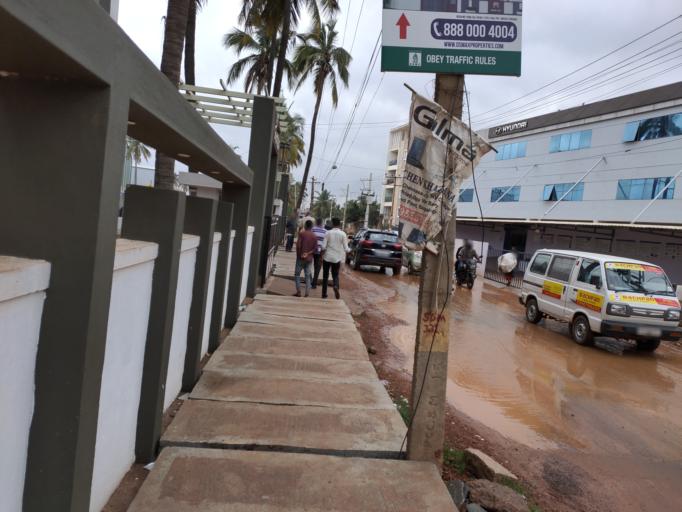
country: IN
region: Karnataka
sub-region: Bangalore Rural
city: Hoskote
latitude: 13.0094
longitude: 77.7597
